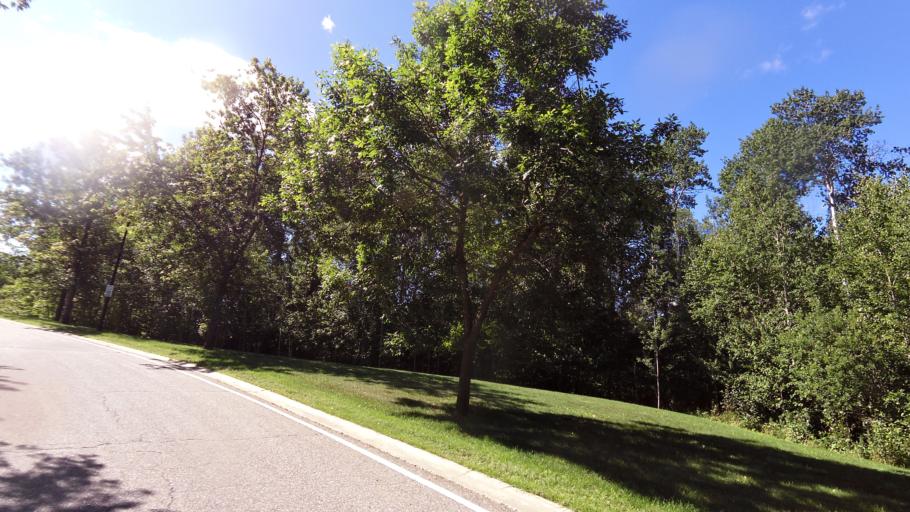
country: CA
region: Ontario
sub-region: Thunder Bay District
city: Thunder Bay
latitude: 48.4856
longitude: -89.1703
